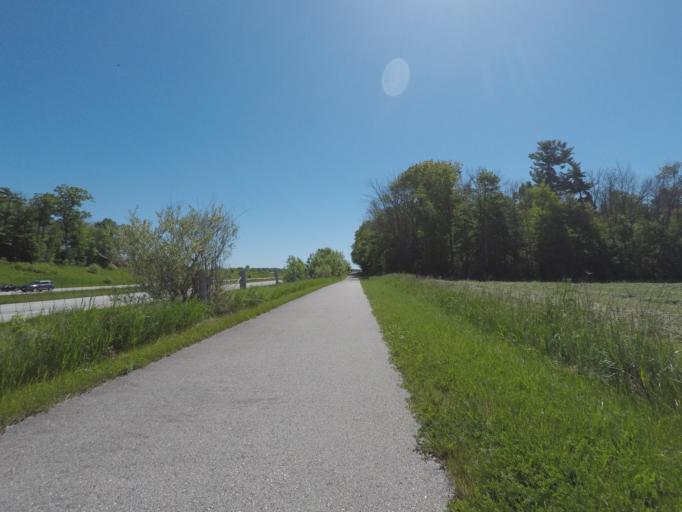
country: US
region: Wisconsin
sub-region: Sheboygan County
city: Sheboygan Falls
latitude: 43.7502
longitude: -87.8105
